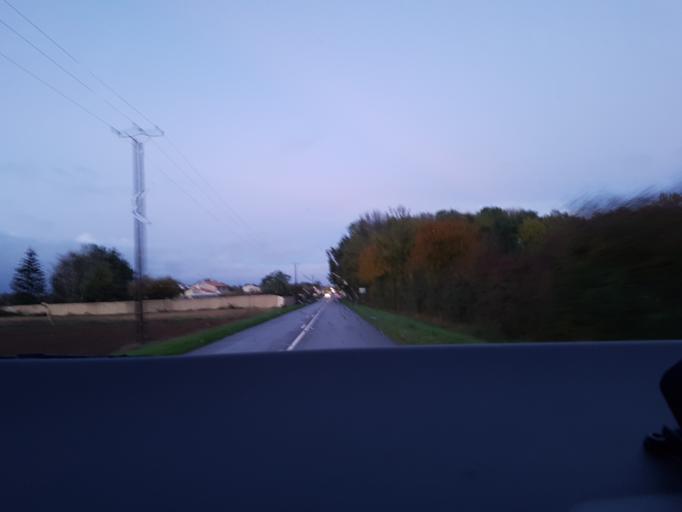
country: FR
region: Poitou-Charentes
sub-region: Departement des Deux-Sevres
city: Lezay
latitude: 46.2579
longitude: -0.0194
